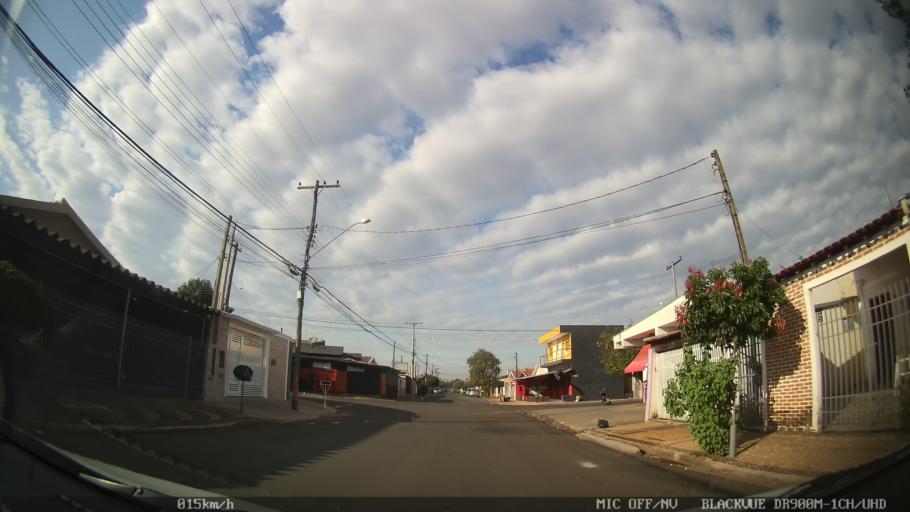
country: BR
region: Sao Paulo
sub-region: Americana
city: Americana
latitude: -22.7283
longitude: -47.3622
